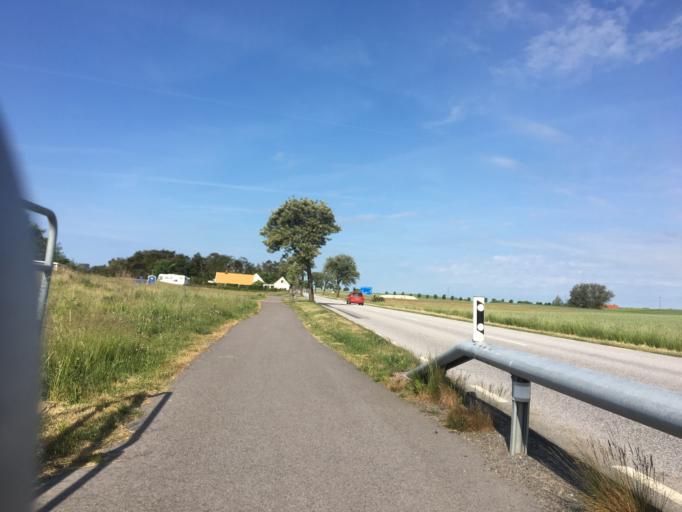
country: SE
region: Skane
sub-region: Skurups Kommun
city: Skivarp
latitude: 55.4184
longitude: 13.6445
